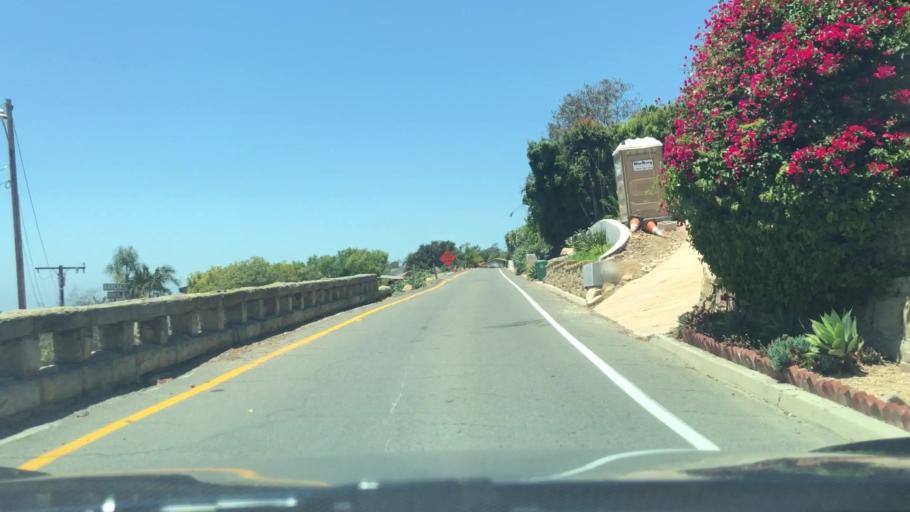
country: US
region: California
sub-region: Santa Barbara County
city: Santa Barbara
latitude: 34.4363
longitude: -119.6903
